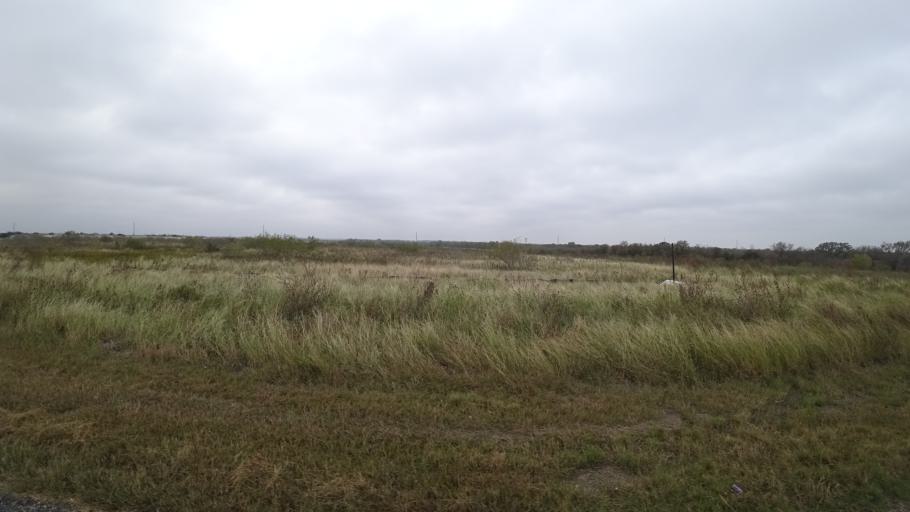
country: US
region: Texas
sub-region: Travis County
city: Pflugerville
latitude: 30.4150
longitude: -97.6112
